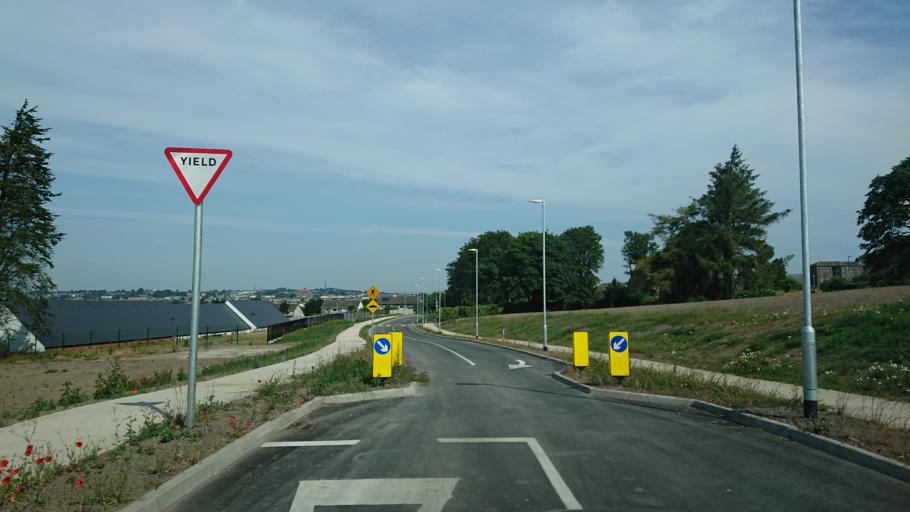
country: IE
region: Munster
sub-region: Waterford
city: Waterford
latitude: 52.2444
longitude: -7.1048
